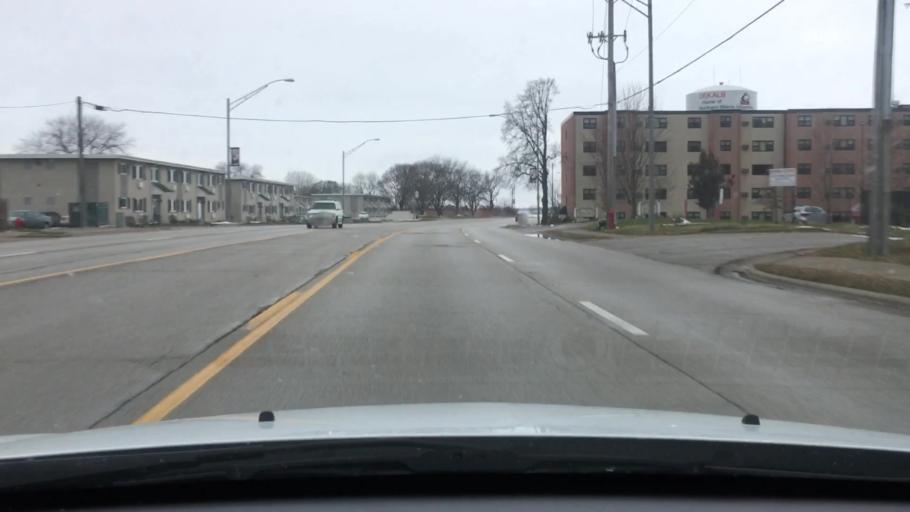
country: US
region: Illinois
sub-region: DeKalb County
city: DeKalb
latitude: 41.9308
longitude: -88.7787
